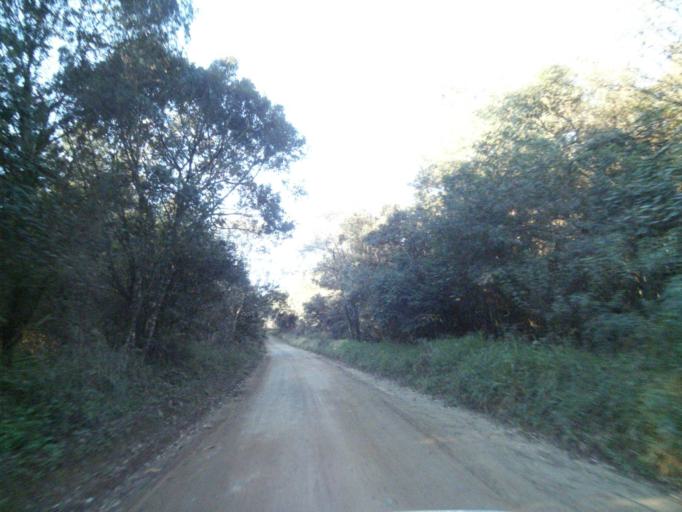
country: BR
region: Parana
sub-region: Tibagi
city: Tibagi
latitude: -24.5319
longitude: -50.5995
